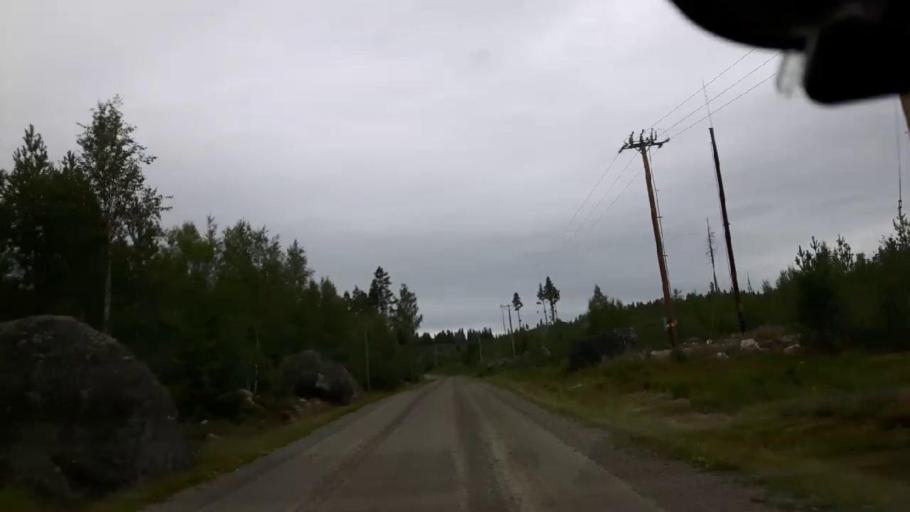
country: SE
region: Vaesternorrland
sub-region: Ange Kommun
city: Fransta
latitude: 62.7912
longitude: 16.0404
